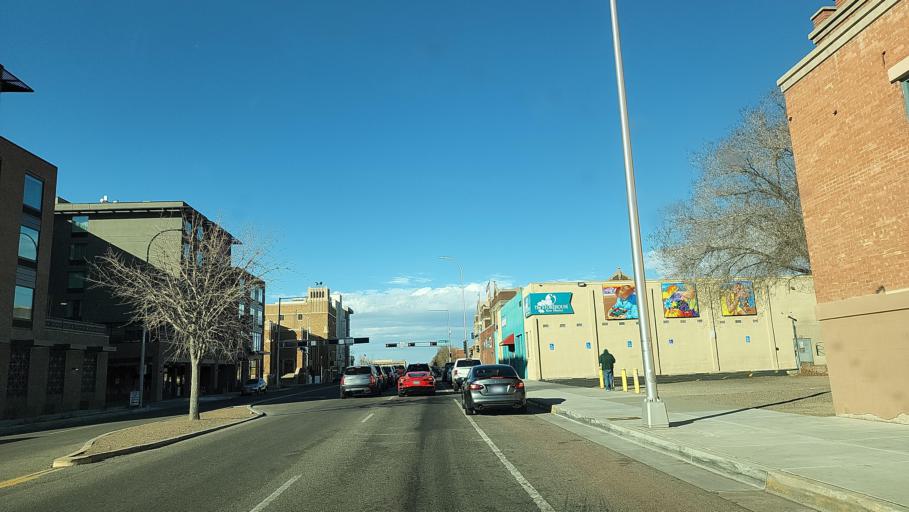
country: US
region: New Mexico
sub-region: Bernalillo County
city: Albuquerque
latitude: 35.0828
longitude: -106.6447
